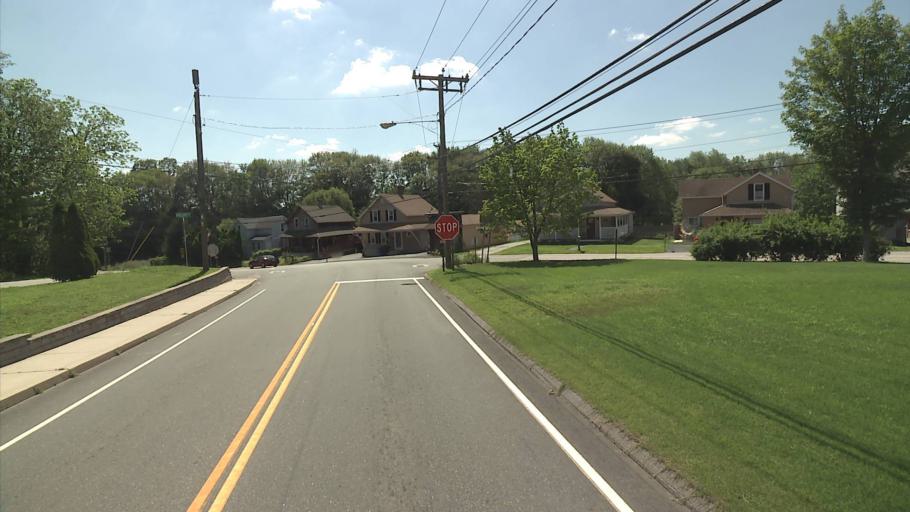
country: US
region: Connecticut
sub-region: Windham County
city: Plainfield Village
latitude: 41.6799
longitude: -71.9247
